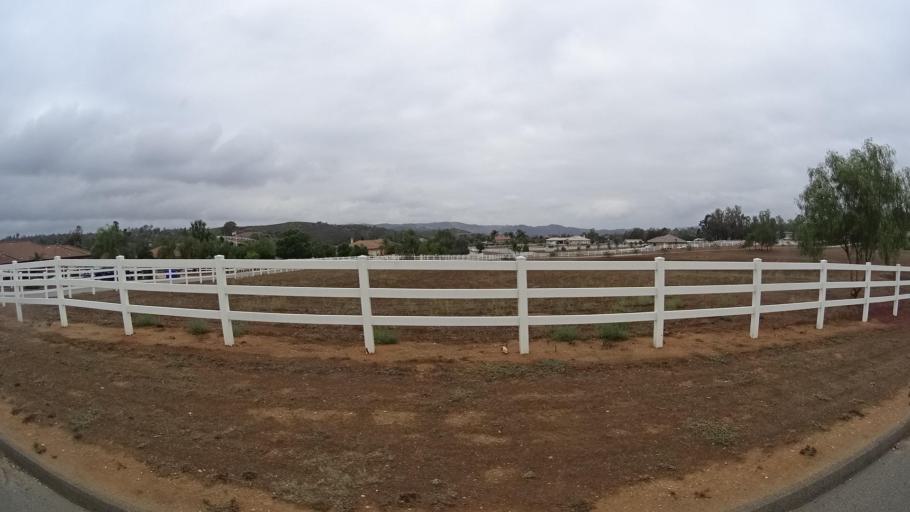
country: US
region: California
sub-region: San Diego County
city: Ramona
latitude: 33.0679
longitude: -116.8717
